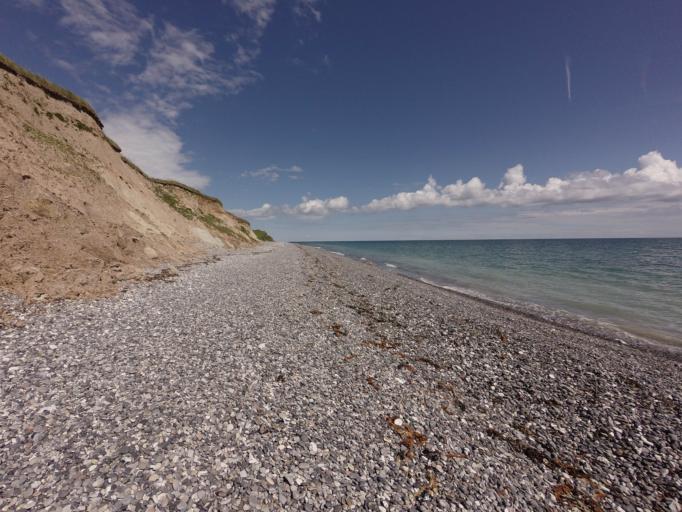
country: DK
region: Central Jutland
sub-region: Norddjurs Kommune
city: Grenaa
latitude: 56.5028
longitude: 10.8683
